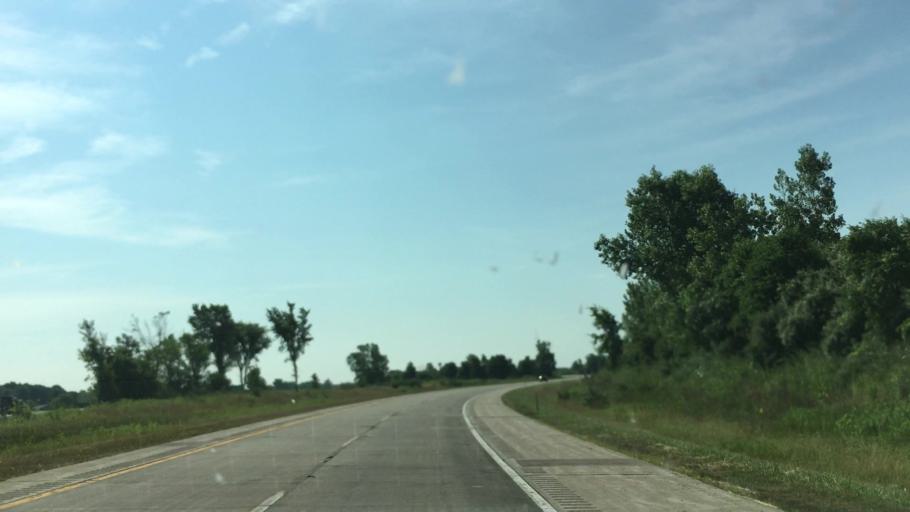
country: US
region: Michigan
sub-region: Clinton County
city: Wacousta
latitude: 42.7959
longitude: -84.6878
